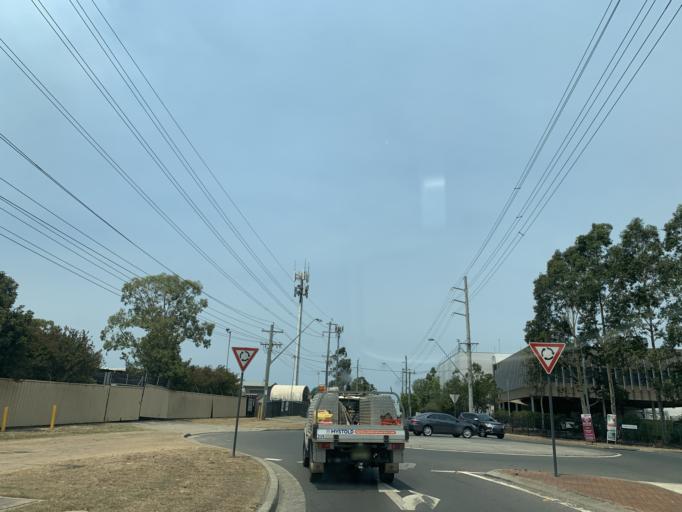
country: AU
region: New South Wales
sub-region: Holroyd
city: Girraween
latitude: -33.7743
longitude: 150.9475
